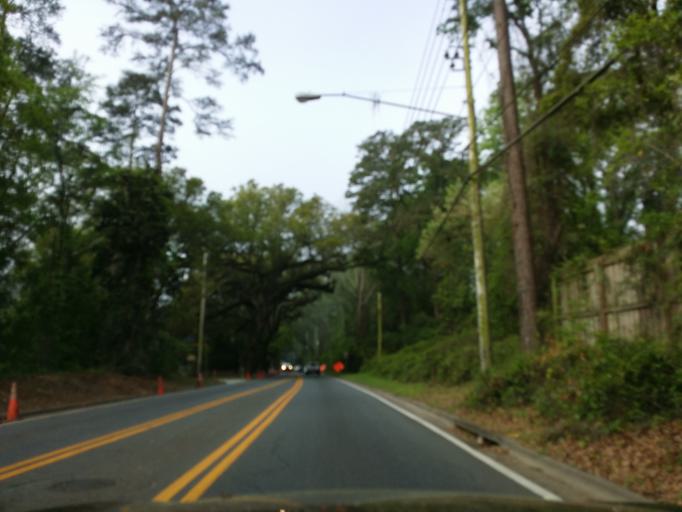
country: US
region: Florida
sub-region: Leon County
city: Tallahassee
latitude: 30.4727
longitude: -84.2453
